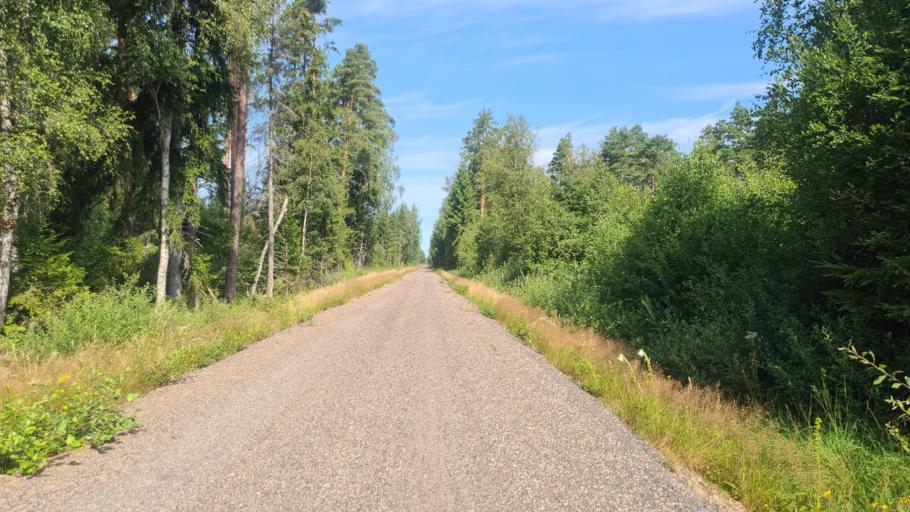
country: SE
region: Kronoberg
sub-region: Ljungby Kommun
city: Lagan
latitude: 56.9623
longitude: 13.9546
